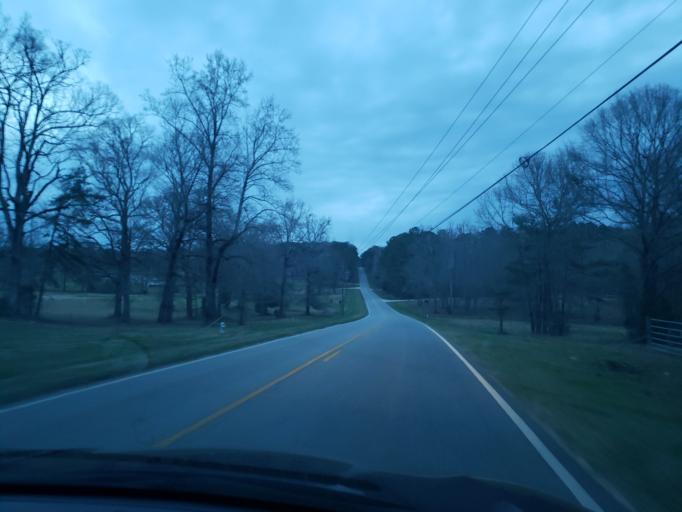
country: US
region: Alabama
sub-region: Lee County
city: Auburn
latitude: 32.6434
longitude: -85.4590
